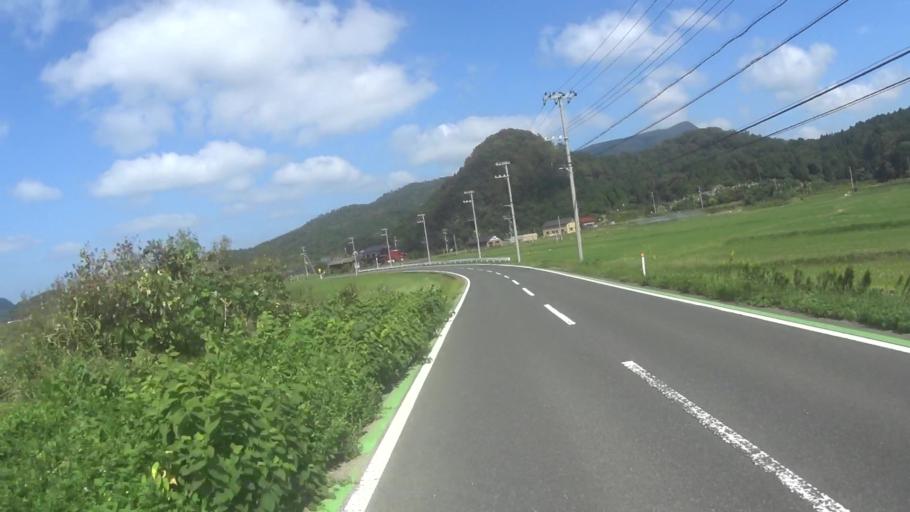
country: JP
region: Kyoto
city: Miyazu
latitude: 35.7163
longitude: 135.1081
